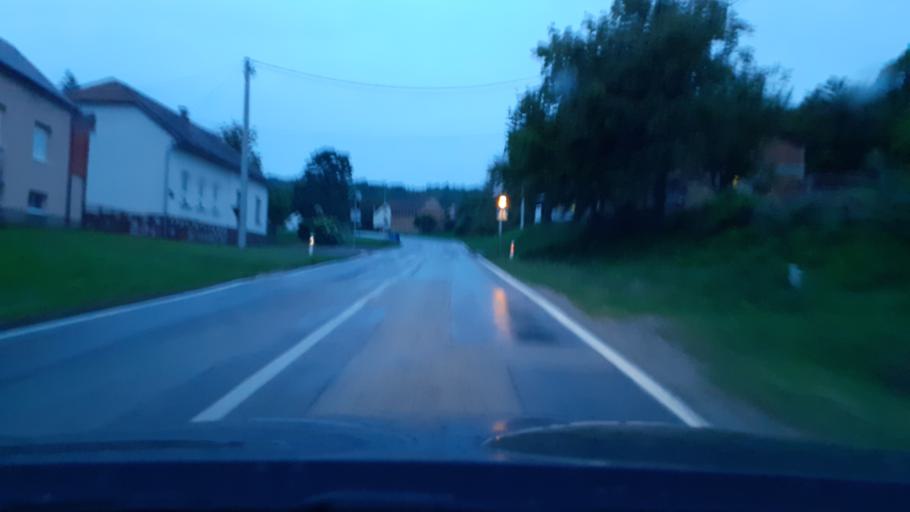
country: HR
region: Pozesko-Slavonska
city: Bilice
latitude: 45.2191
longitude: 17.8527
